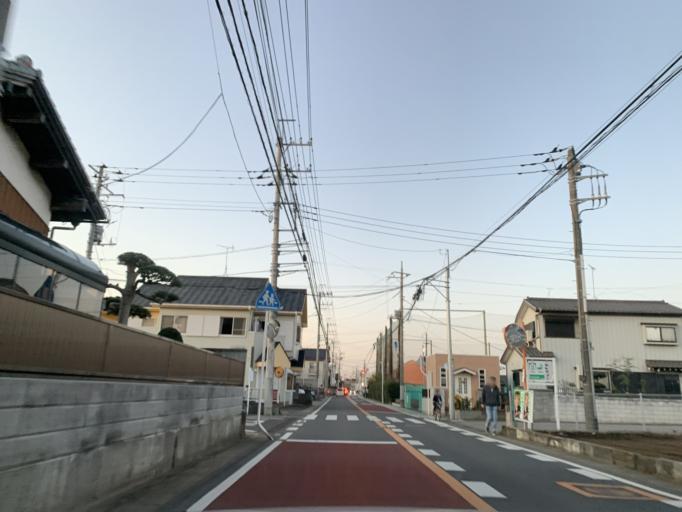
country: JP
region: Chiba
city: Nagareyama
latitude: 35.9064
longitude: 139.9041
